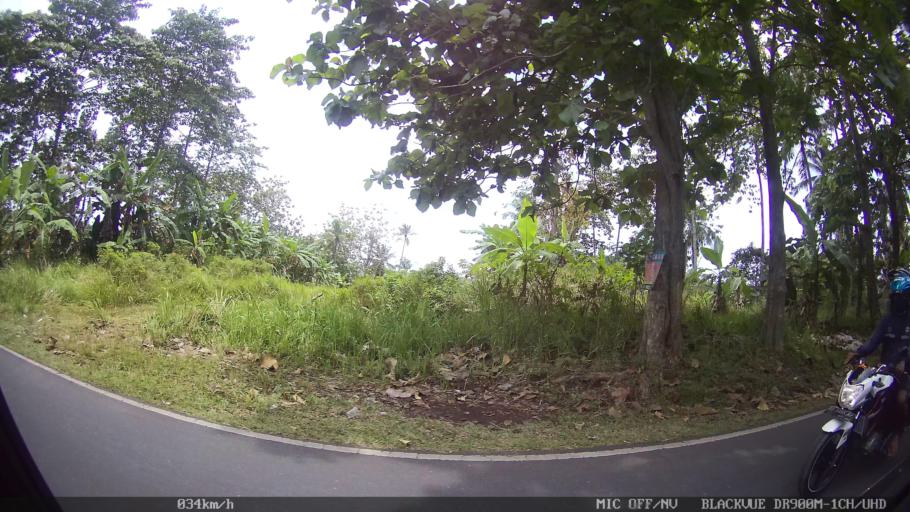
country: ID
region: Lampung
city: Bandarlampung
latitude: -5.4162
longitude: 105.2339
